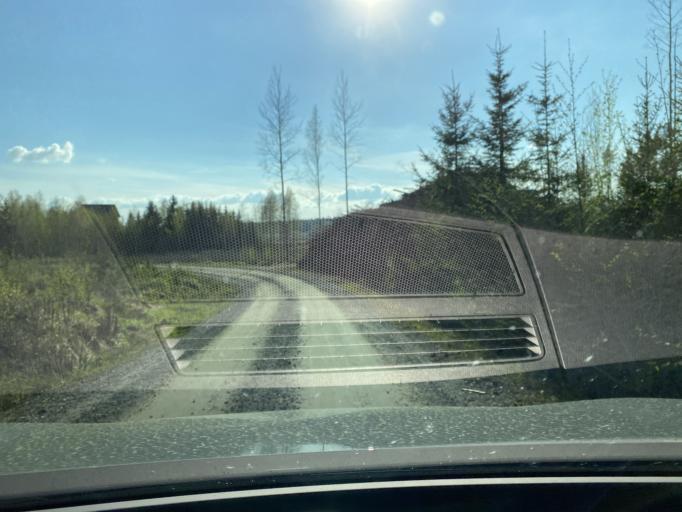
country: FI
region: Pirkanmaa
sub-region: Lounais-Pirkanmaa
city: Punkalaidun
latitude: 61.0343
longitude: 23.2260
